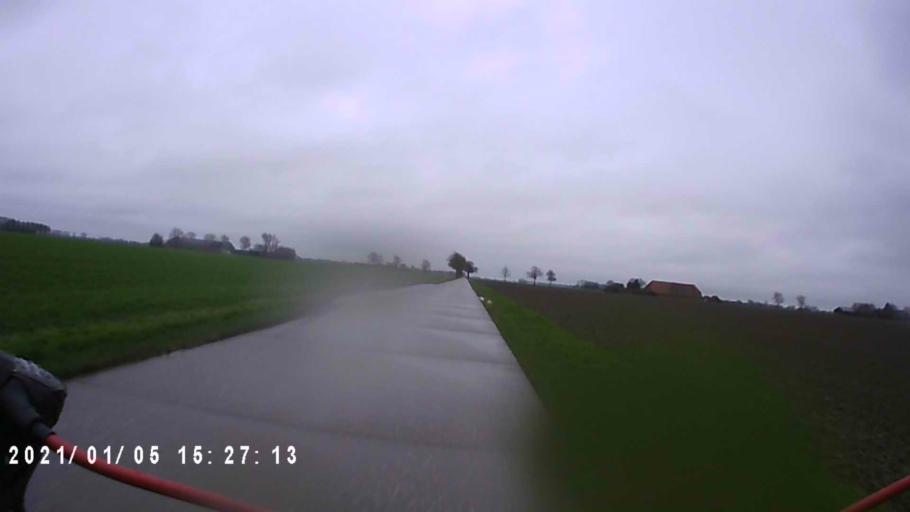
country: DE
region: Lower Saxony
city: Bunde
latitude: 53.2208
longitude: 7.1964
